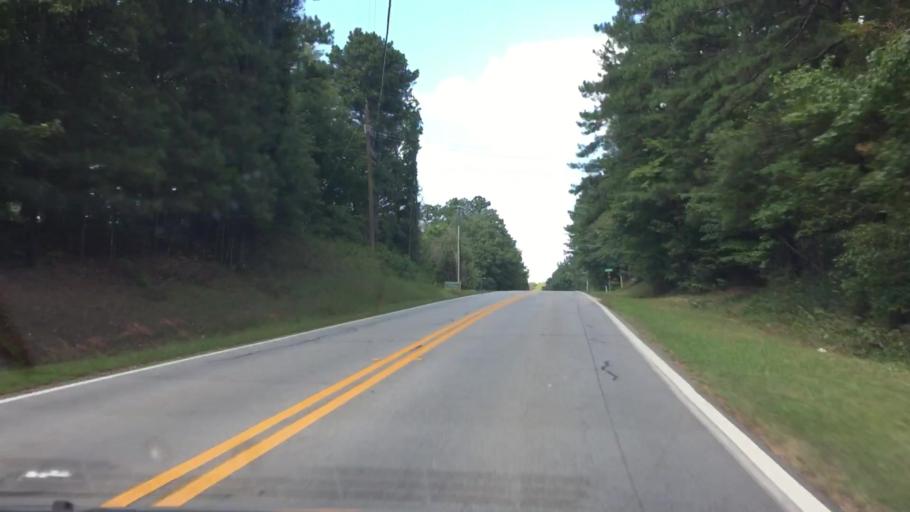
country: US
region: Georgia
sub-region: Fayette County
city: Shannon
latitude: 33.3971
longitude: -84.4953
